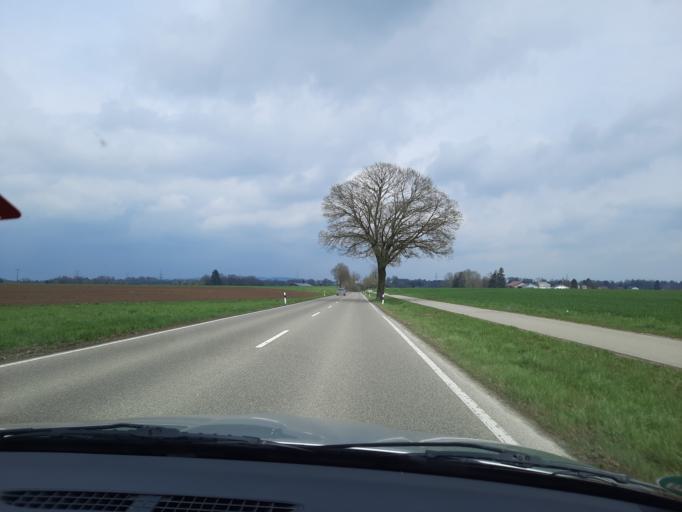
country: DE
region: Bavaria
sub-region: Swabia
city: Buxheim
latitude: 47.9688
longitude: 10.1437
